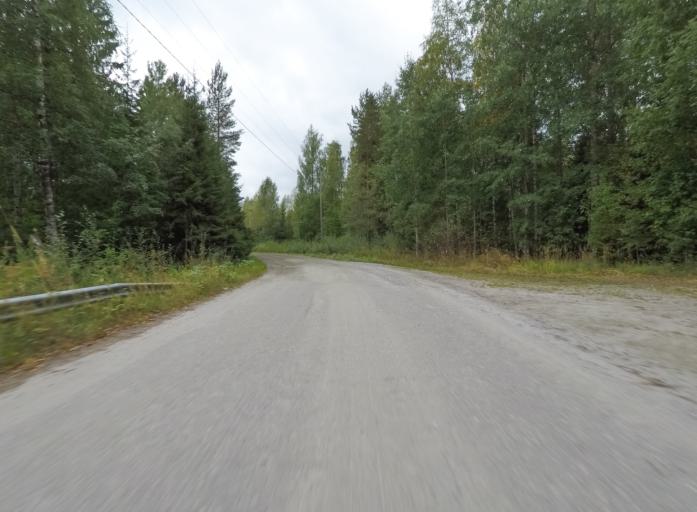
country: FI
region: Central Finland
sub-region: Jyvaeskylae
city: Hankasalmi
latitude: 62.4302
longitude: 26.6469
